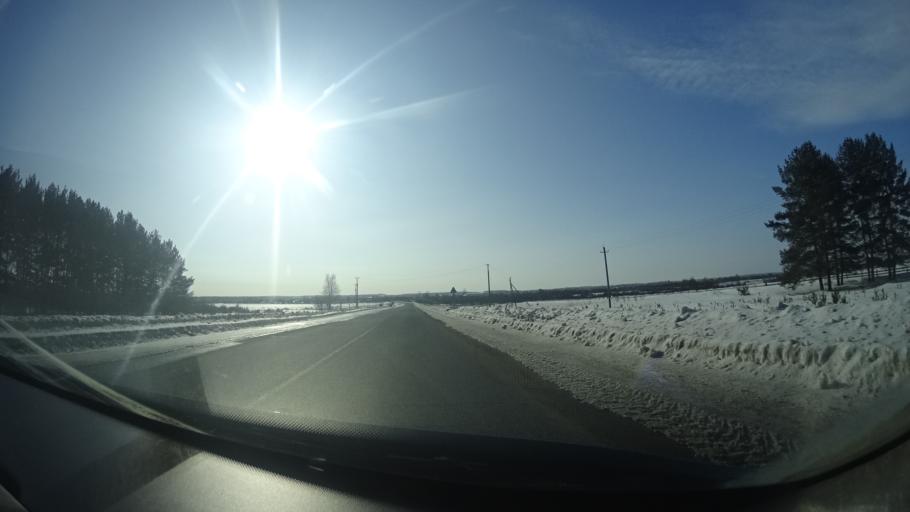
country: RU
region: Perm
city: Kuyeda
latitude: 56.4646
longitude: 55.5930
